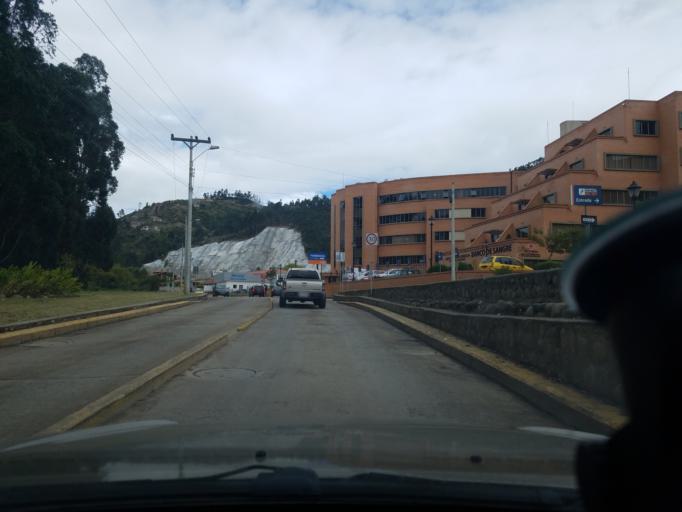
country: EC
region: Azuay
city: Cuenca
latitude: -2.8923
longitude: -78.9617
